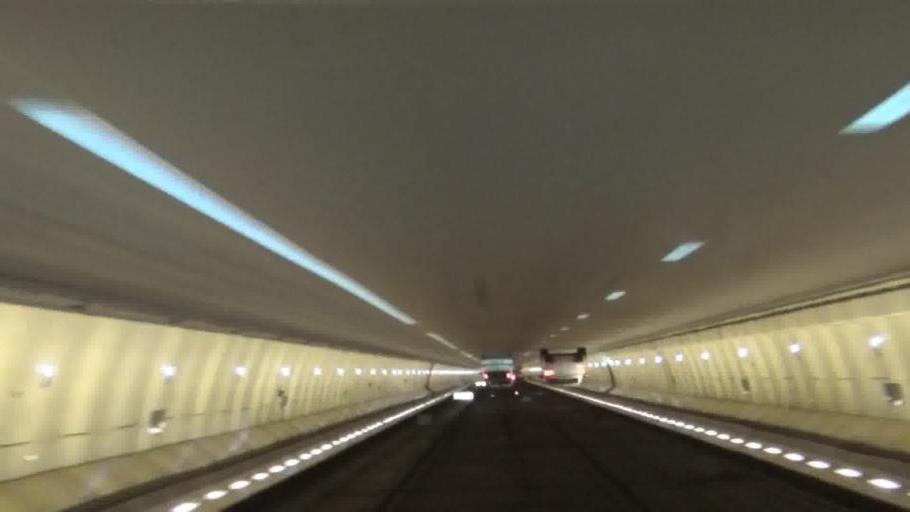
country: FR
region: Ile-de-France
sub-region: Departement des Yvelines
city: La Celle-Saint-Cloud
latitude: 48.8531
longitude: 2.1531
